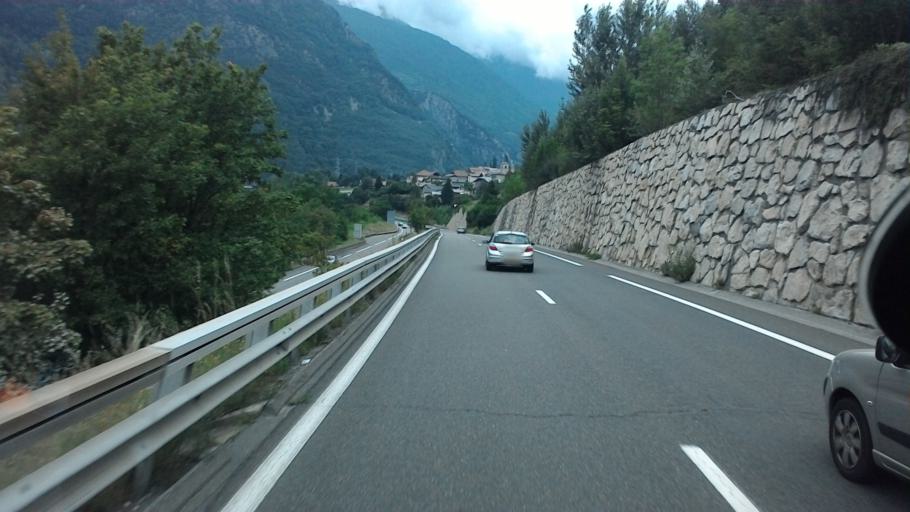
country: FR
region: Rhone-Alpes
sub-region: Departement de la Savoie
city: Aigueblanche
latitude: 45.5114
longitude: 6.5006
